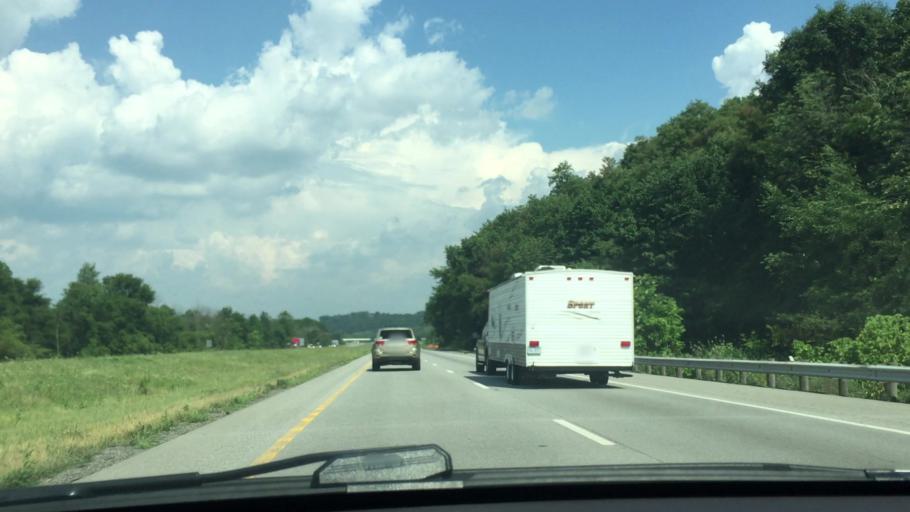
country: US
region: Ohio
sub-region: Guernsey County
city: Cambridge
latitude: 40.0077
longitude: -81.6398
